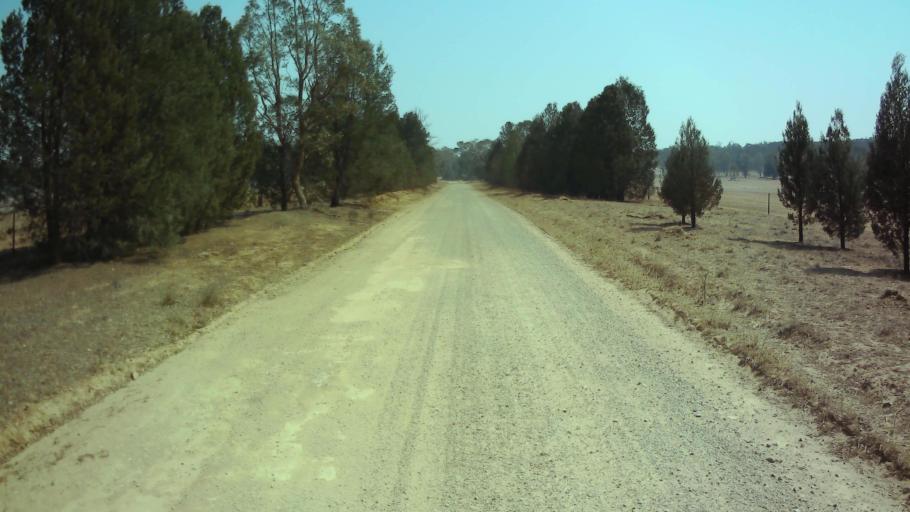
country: AU
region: New South Wales
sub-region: Weddin
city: Grenfell
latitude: -33.6698
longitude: 148.2749
